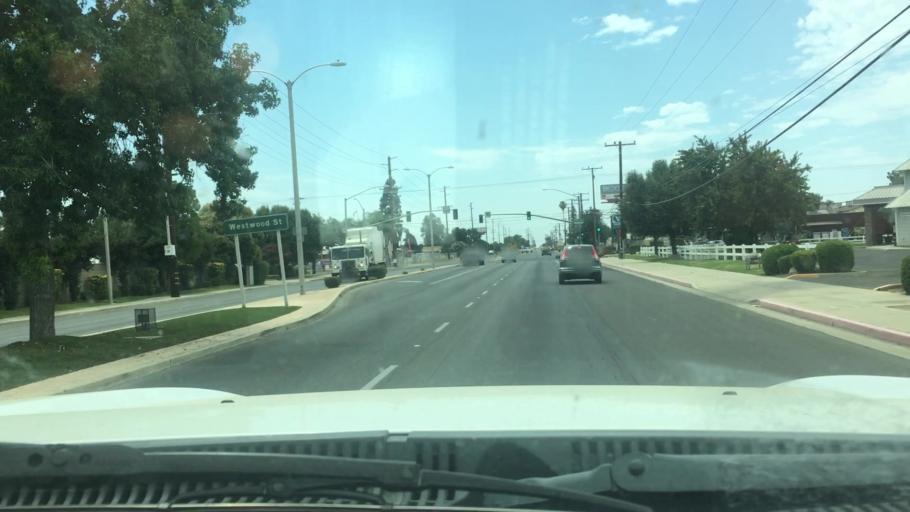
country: US
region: California
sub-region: Tulare County
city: Porterville
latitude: 36.0658
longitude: -119.0695
